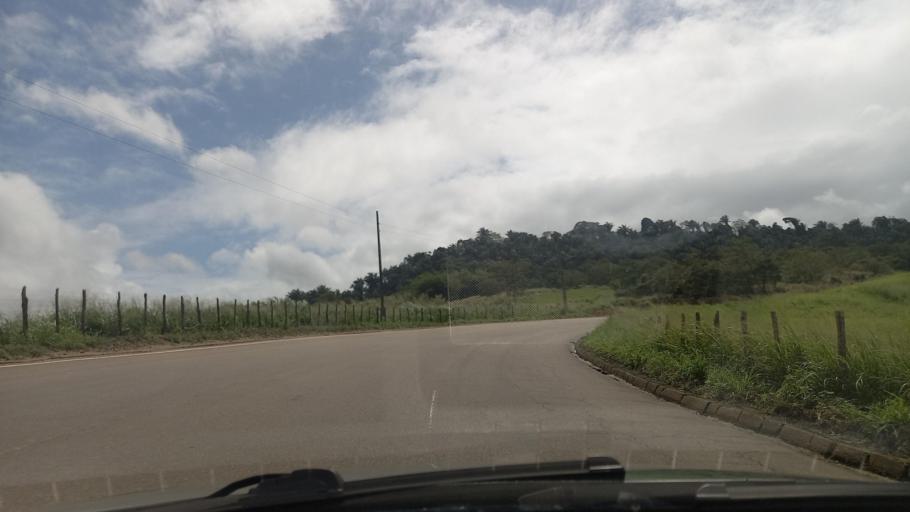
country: BR
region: Alagoas
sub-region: Campo Alegre
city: Campo Alegre
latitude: -9.8122
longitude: -36.2222
